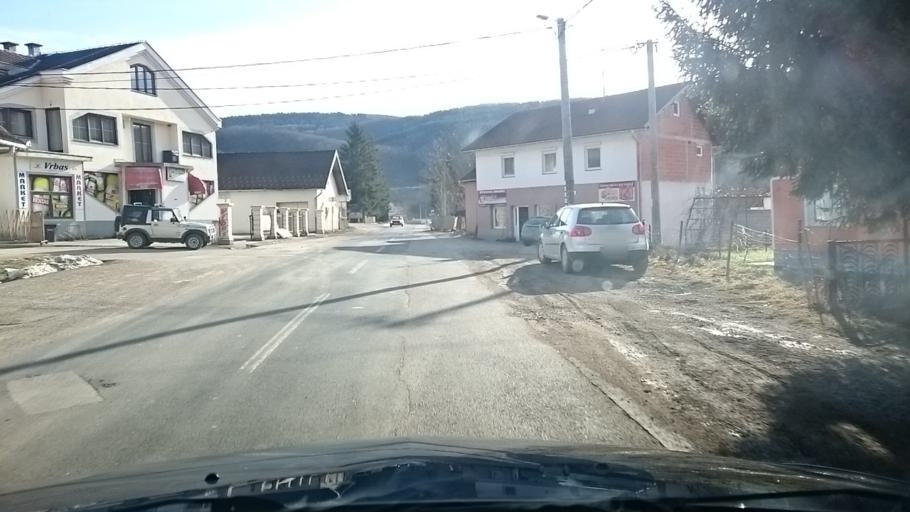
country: BA
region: Republika Srpska
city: Starcevica
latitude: 44.6952
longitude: 17.2072
